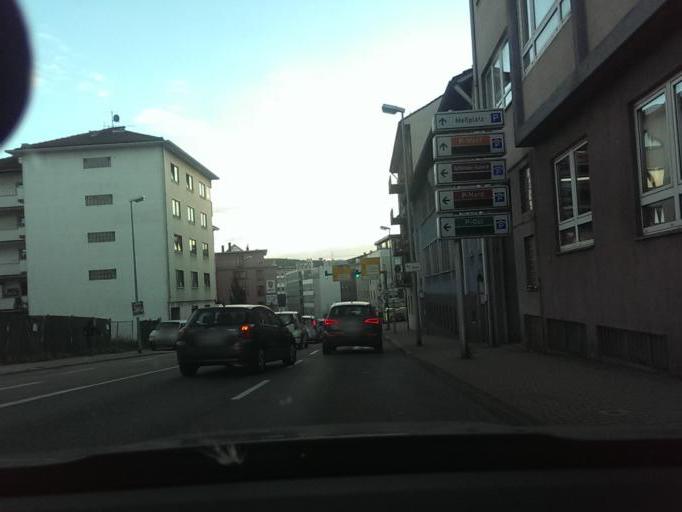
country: DE
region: Baden-Wuerttemberg
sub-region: Karlsruhe Region
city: Pforzheim
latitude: 48.8945
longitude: 8.6942
